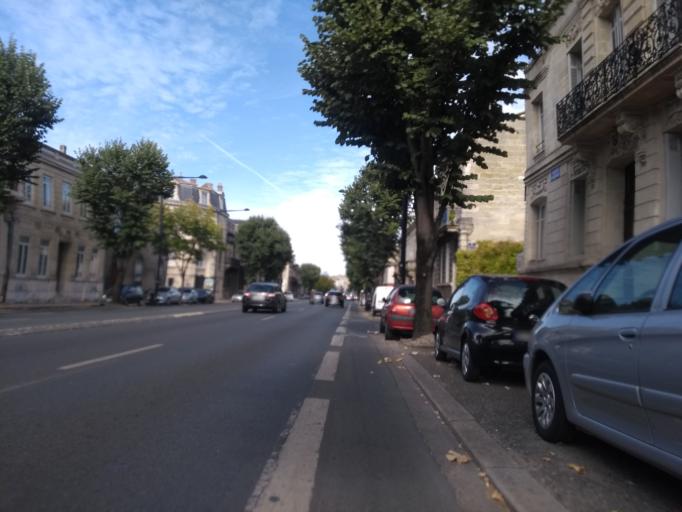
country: FR
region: Aquitaine
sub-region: Departement de la Gironde
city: Bordeaux
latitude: 44.8449
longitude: -0.5989
